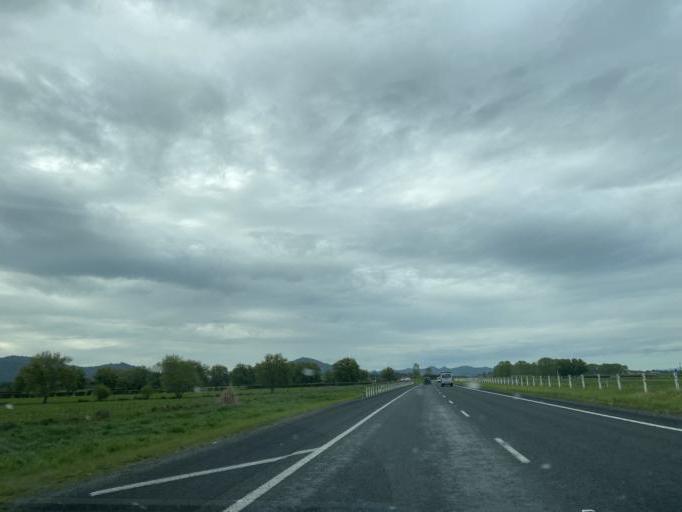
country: NZ
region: Waikato
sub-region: Waikato District
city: Ngaruawahia
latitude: -37.6587
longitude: 175.2057
